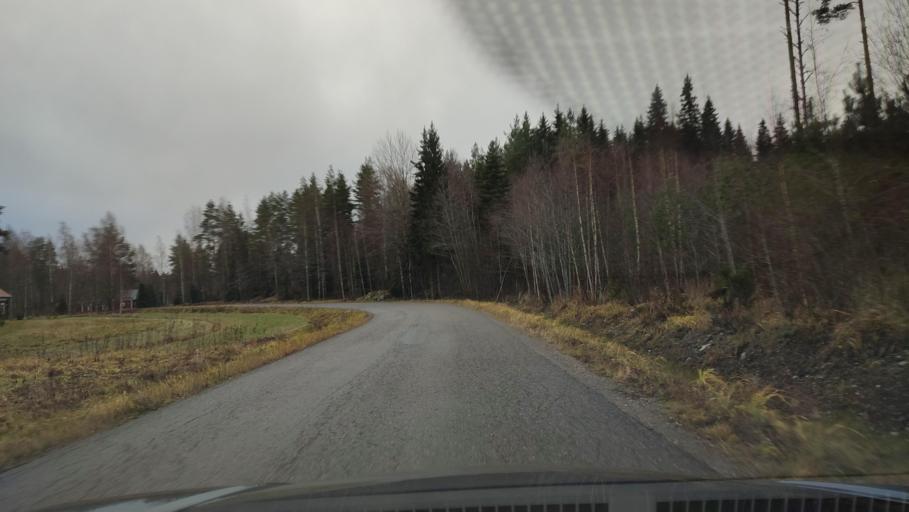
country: FI
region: Southern Ostrobothnia
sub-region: Suupohja
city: Karijoki
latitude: 62.1378
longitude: 21.5726
